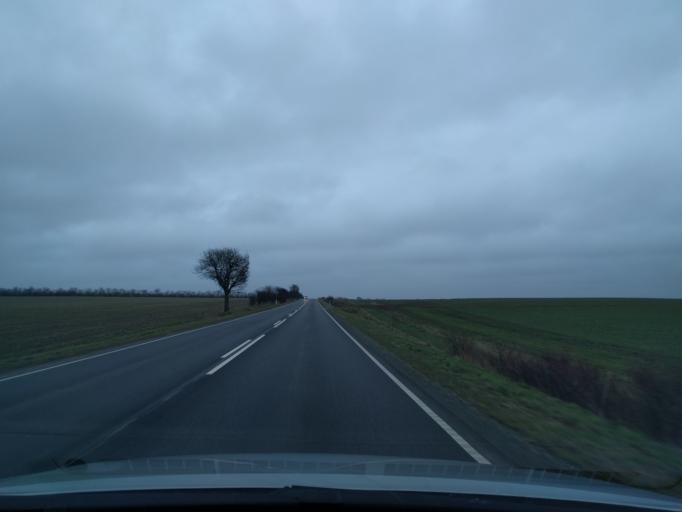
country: DK
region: South Denmark
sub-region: Haderslev Kommune
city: Vojens
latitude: 55.2478
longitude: 9.1840
